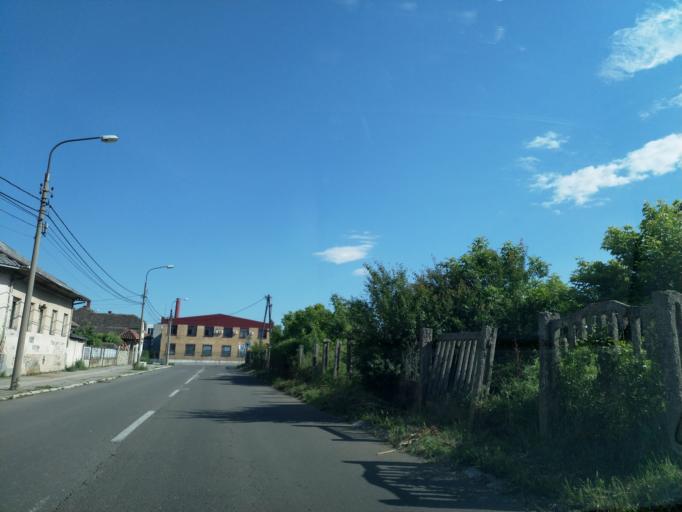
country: RS
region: Central Serbia
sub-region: Pomoravski Okrug
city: Paracin
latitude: 43.8622
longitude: 21.4013
